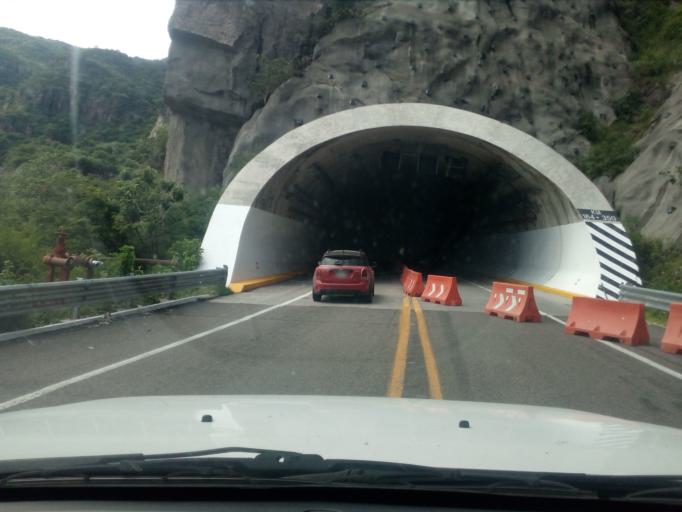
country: MX
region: Durango
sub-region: Pueblo Nuevo
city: La Ciudad
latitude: 23.5111
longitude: -105.8019
